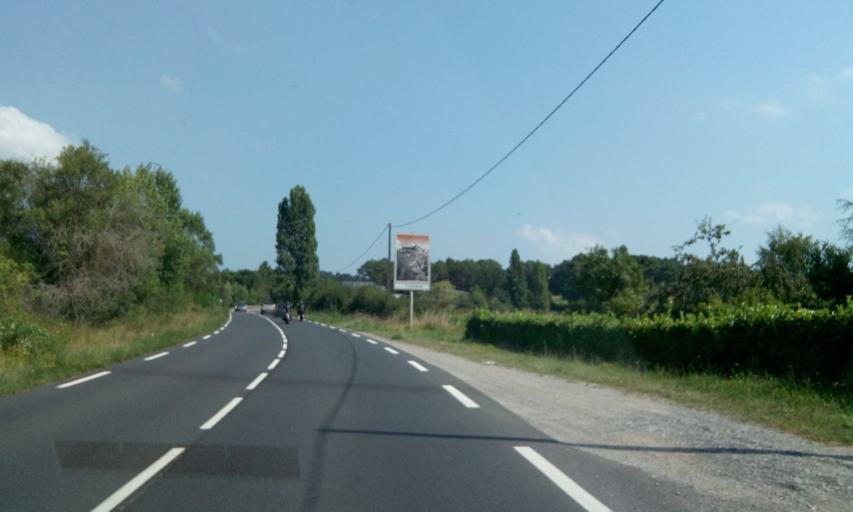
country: FR
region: Limousin
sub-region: Departement de la Correze
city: Cosnac
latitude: 45.1098
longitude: 1.5668
